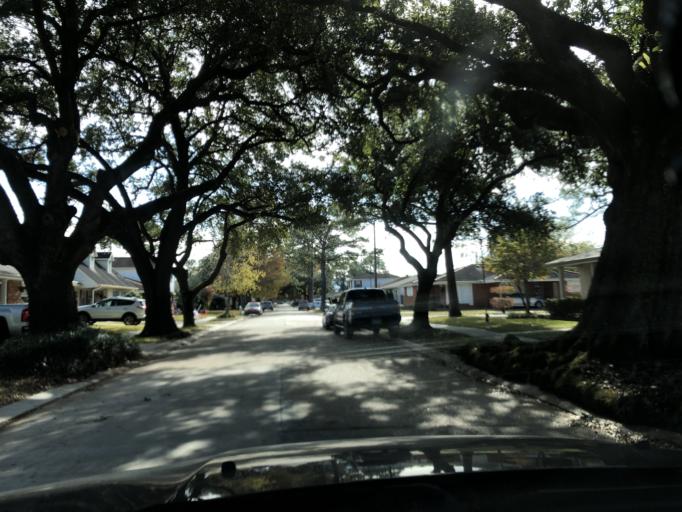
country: US
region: Louisiana
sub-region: Jefferson Parish
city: Metairie Terrace
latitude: 29.9916
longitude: -90.1671
